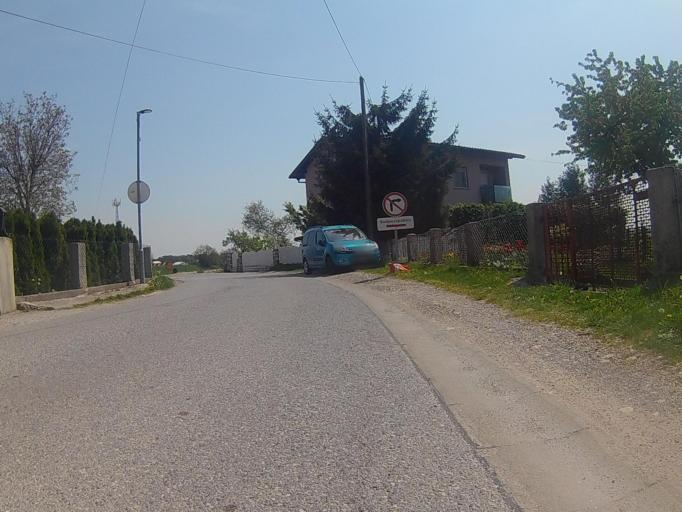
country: SI
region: Miklavz na Dravskem Polju
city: Miklavz na Dravskem Polju
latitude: 46.5021
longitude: 15.7046
